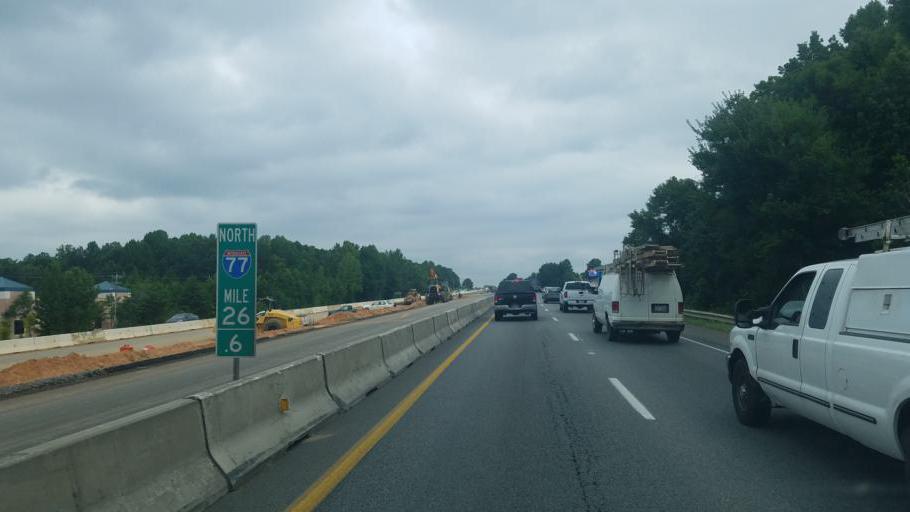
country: US
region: North Carolina
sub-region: Mecklenburg County
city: Cornelius
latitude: 35.4677
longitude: -80.8752
